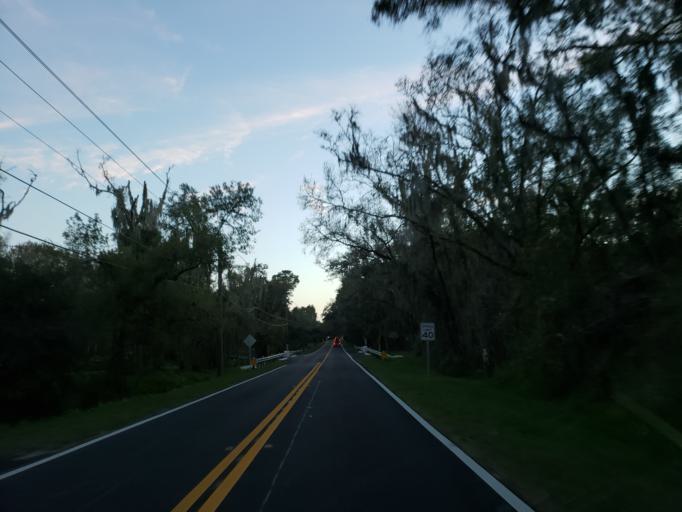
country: US
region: Florida
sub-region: Hillsborough County
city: Fish Hawk
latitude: 27.8422
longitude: -82.1999
